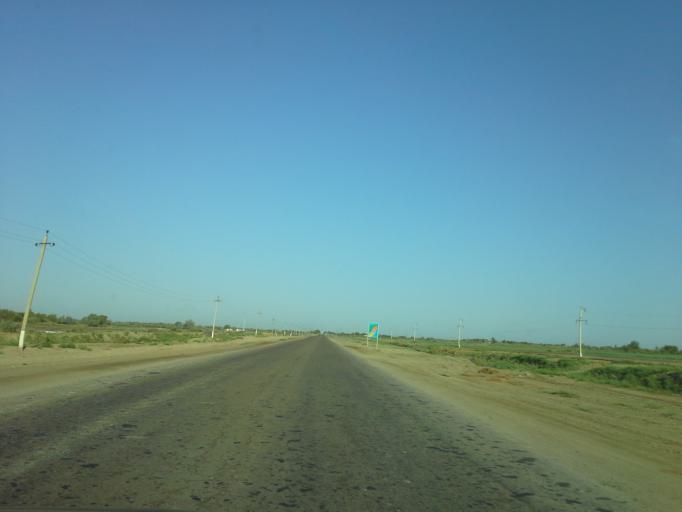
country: UZ
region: Karakalpakstan
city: Khujayli
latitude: 42.2233
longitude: 59.4830
